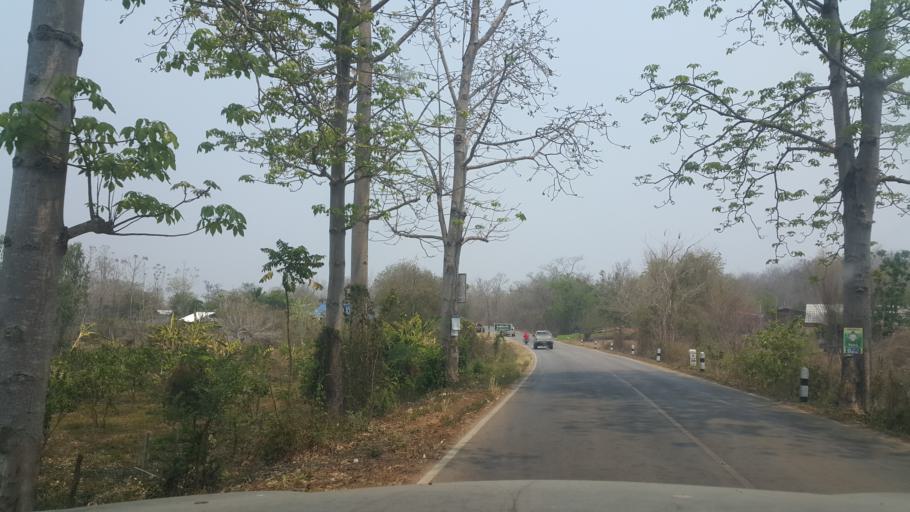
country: TH
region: Lampang
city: Soem Ngam
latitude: 18.0224
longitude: 99.2248
